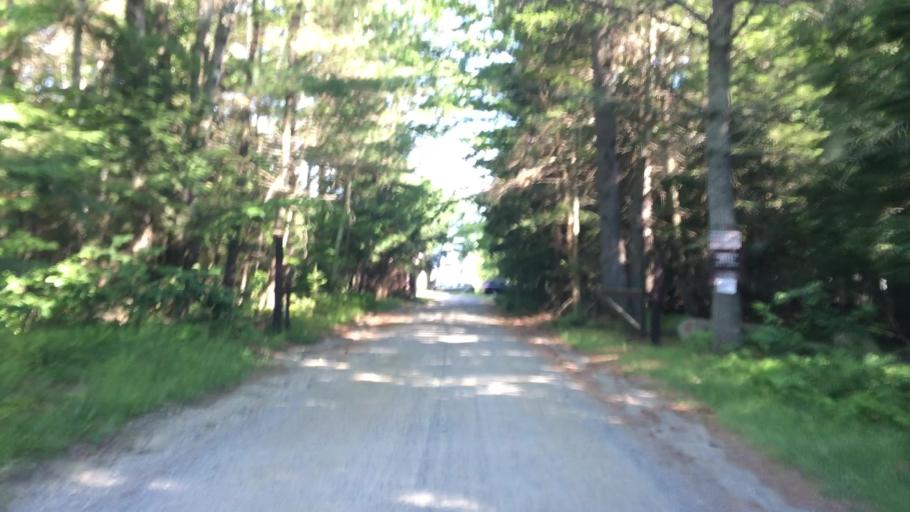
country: US
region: Maine
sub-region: Penobscot County
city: Enfield
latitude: 45.2713
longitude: -68.5600
